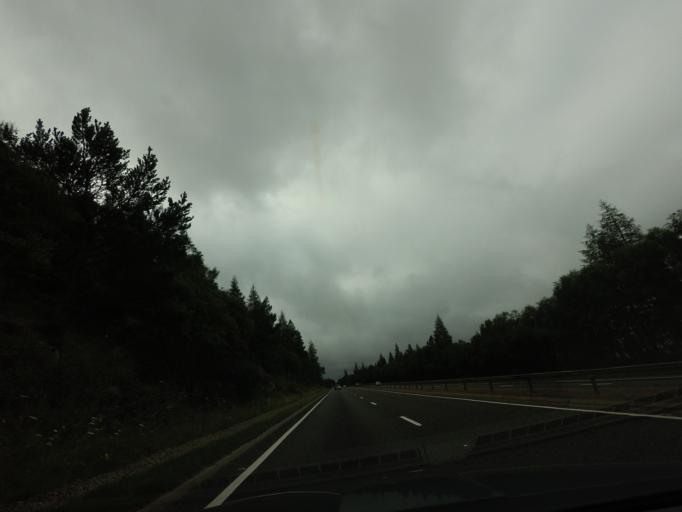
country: GB
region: Scotland
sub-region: Highland
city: Aviemore
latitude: 57.3273
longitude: -3.9780
